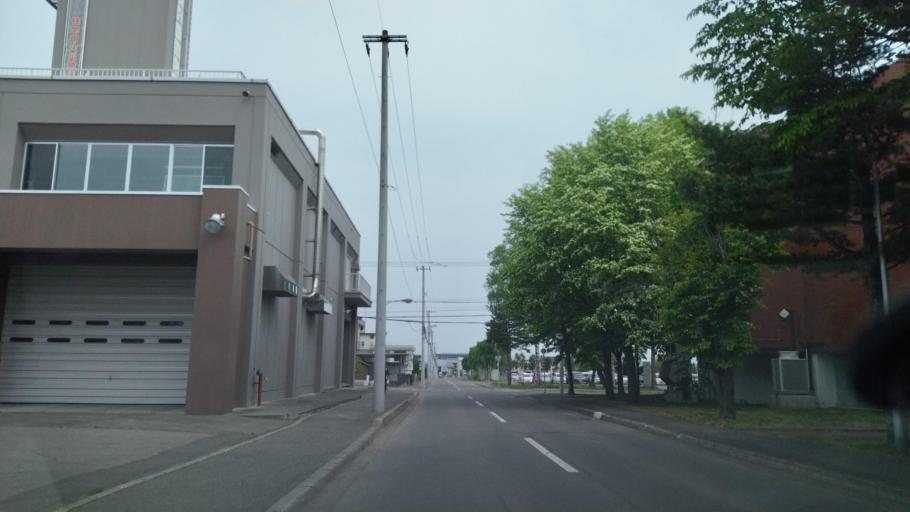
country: JP
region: Hokkaido
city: Obihiro
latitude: 42.9127
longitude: 143.0519
